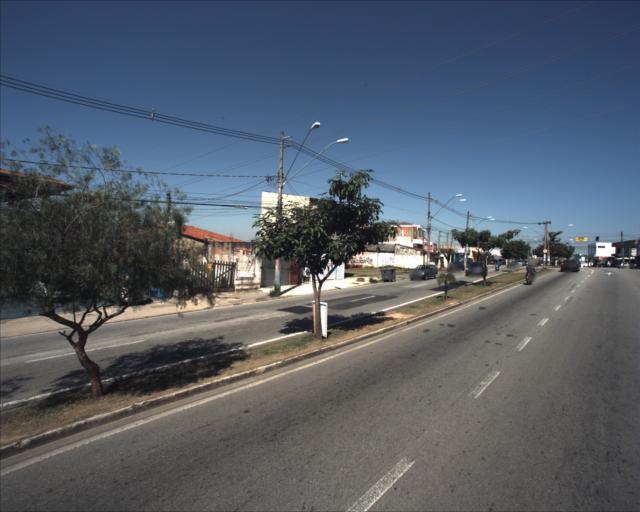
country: BR
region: Sao Paulo
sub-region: Sorocaba
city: Sorocaba
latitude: -23.5024
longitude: -47.5093
